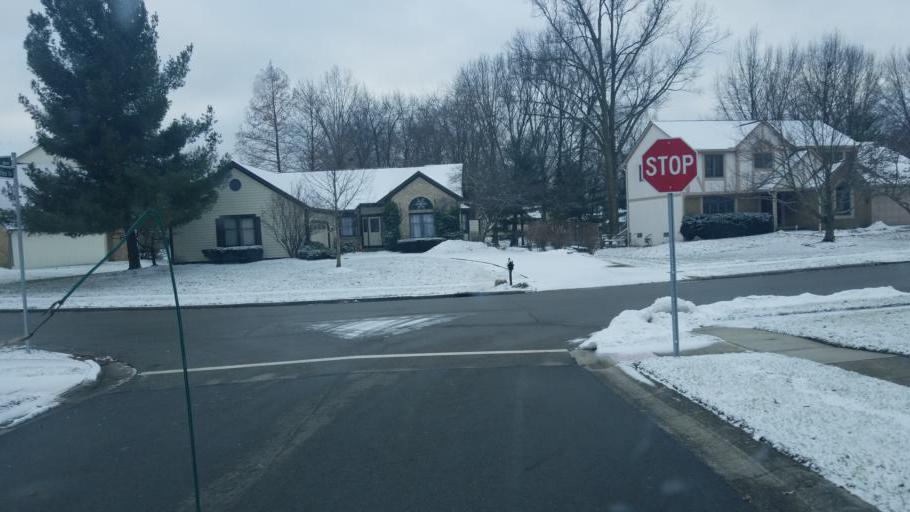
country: US
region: Ohio
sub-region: Franklin County
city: Gahanna
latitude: 40.0445
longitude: -82.8507
